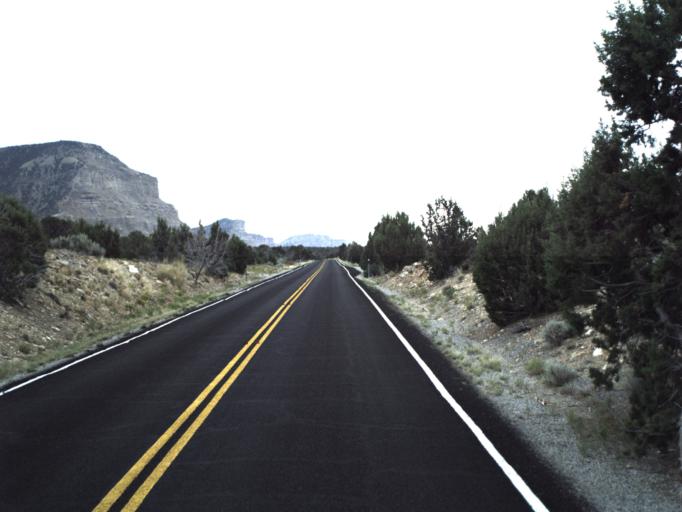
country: US
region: Utah
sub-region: Carbon County
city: East Carbon City
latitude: 39.4590
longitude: -110.3884
